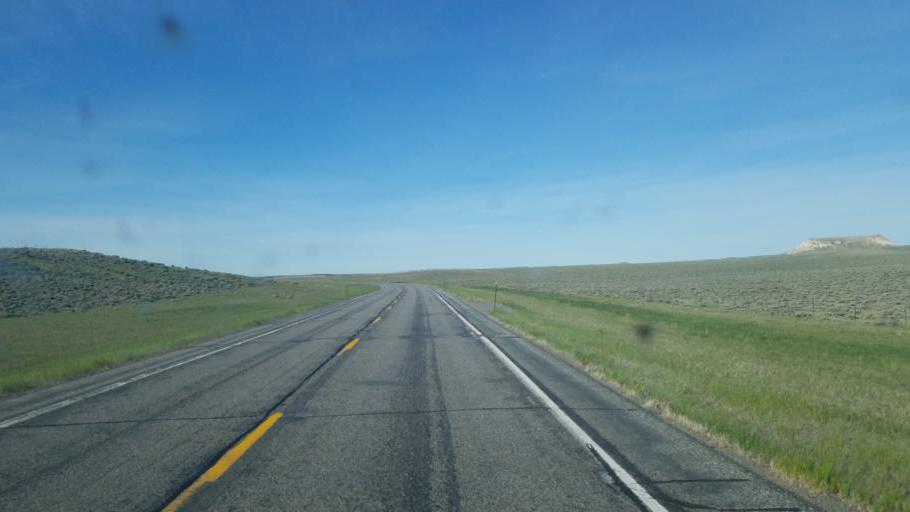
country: US
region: Wyoming
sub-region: Fremont County
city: Riverton
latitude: 42.6509
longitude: -108.1912
